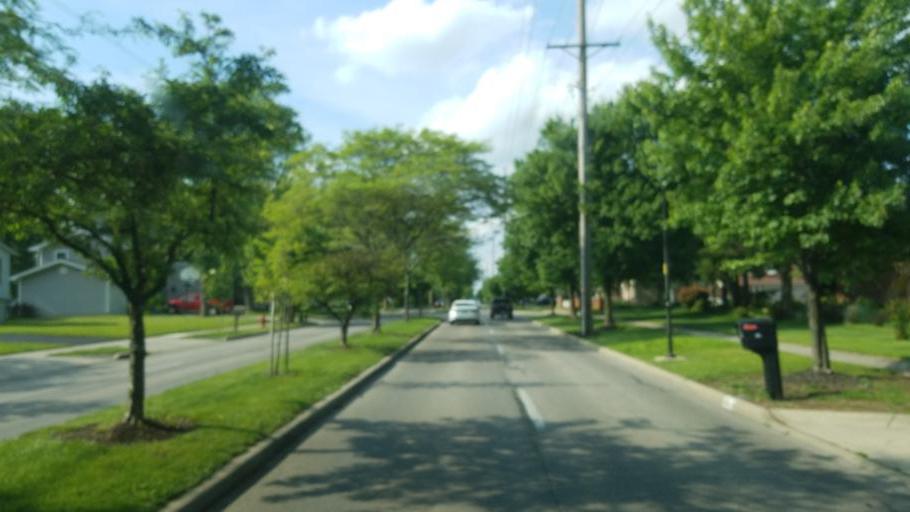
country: US
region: Ohio
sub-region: Franklin County
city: Westerville
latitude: 40.1275
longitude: -82.9032
